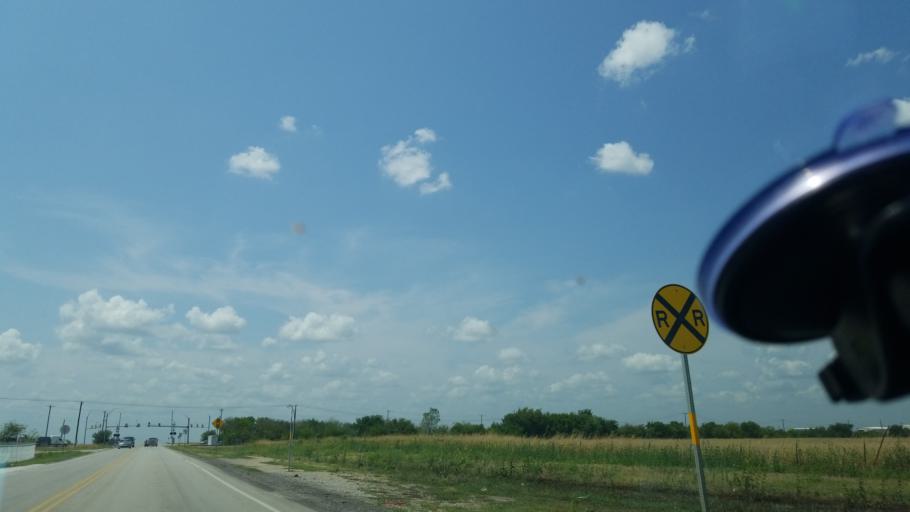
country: US
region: Texas
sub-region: Tarrant County
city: Eagle Mountain
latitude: 32.9245
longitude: -97.4093
